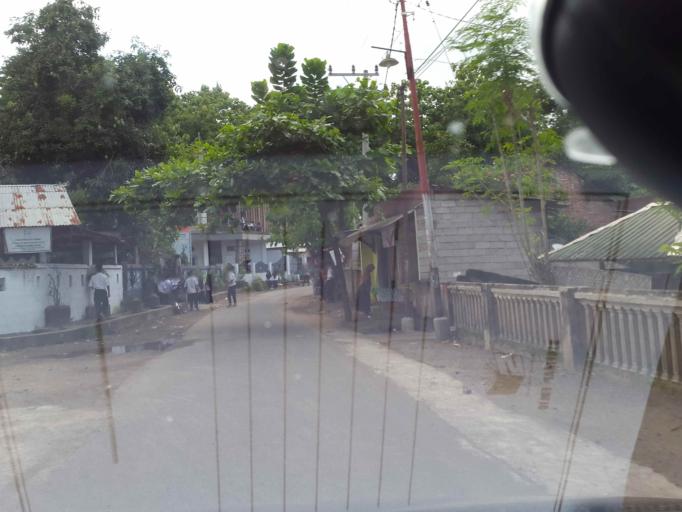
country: ID
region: West Nusa Tenggara
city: Mambalan
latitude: -8.5303
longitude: 116.0820
